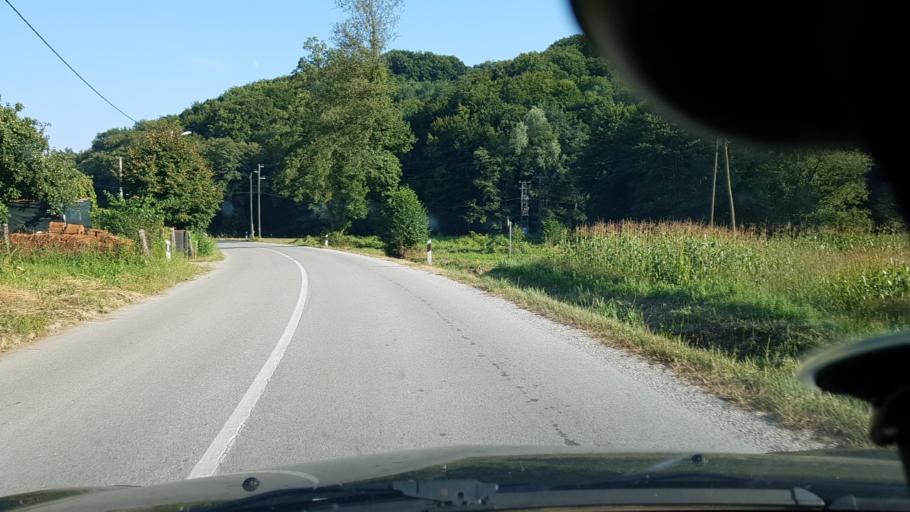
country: SI
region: Bistrica ob Sotli
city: Bistrica ob Sotli
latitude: 46.0392
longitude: 15.7603
